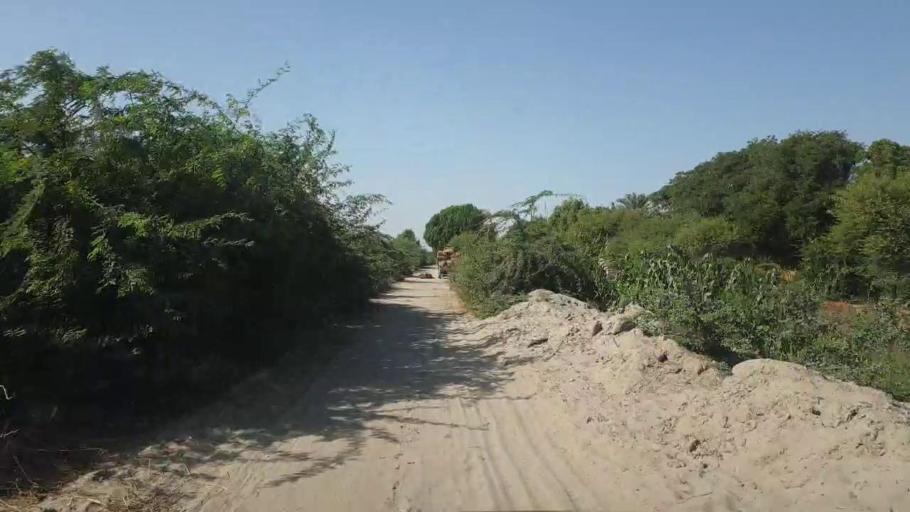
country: PK
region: Sindh
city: Kadhan
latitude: 24.5768
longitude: 68.9840
